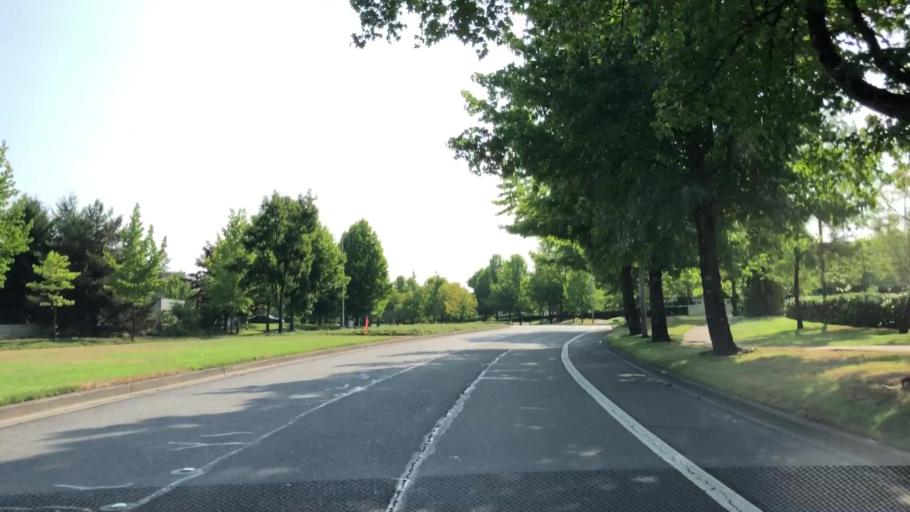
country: US
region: Washington
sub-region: Thurston County
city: Tanglewilde-Thompson Place
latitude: 47.0700
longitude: -122.7603
